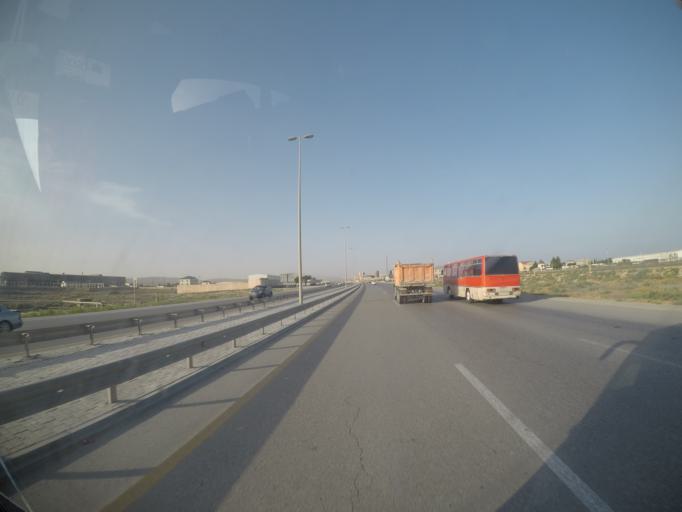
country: AZ
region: Baki
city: Korgoz
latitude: 40.2193
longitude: 49.5604
